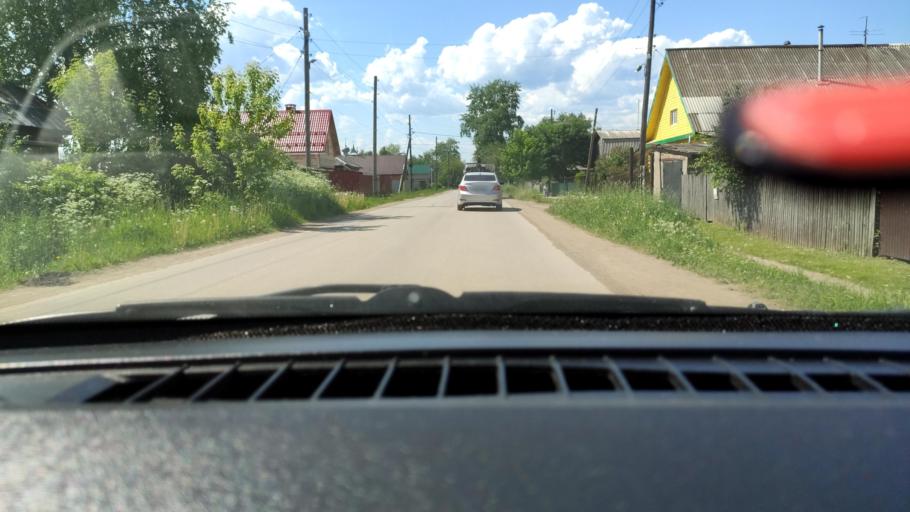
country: RU
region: Perm
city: Sylva
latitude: 58.0332
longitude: 56.7645
